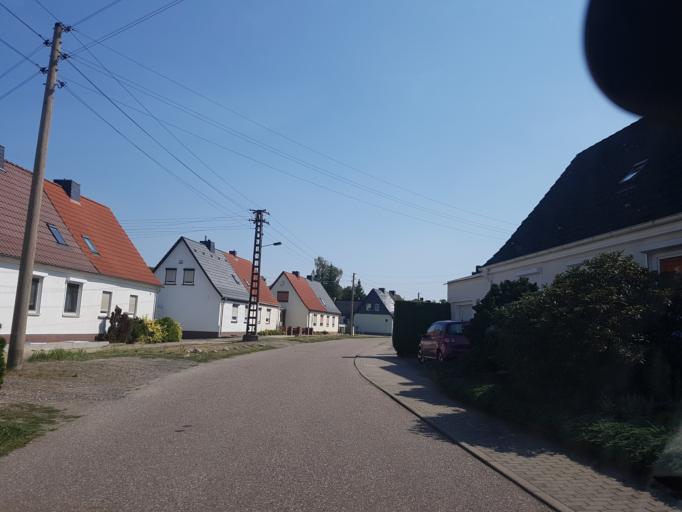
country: DE
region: Saxony-Anhalt
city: Coswig
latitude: 51.8967
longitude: 12.4653
